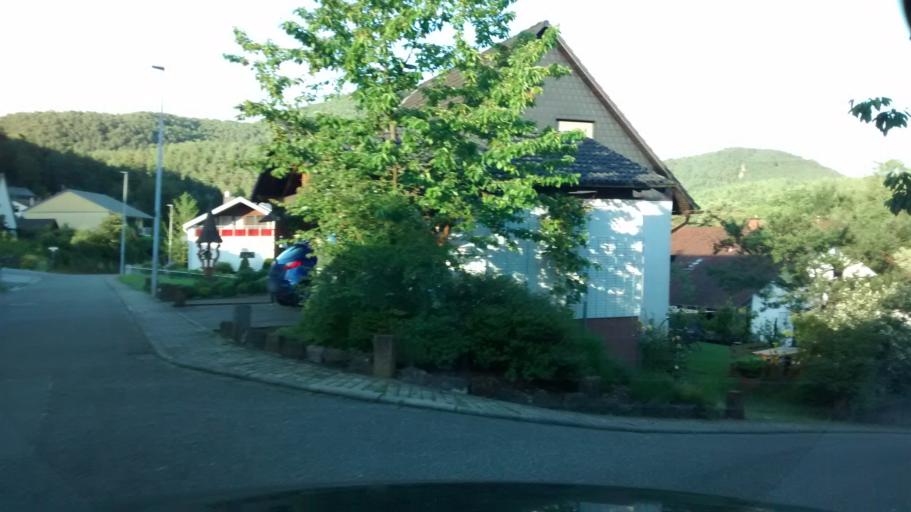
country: DE
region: Rheinland-Pfalz
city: Erfweiler
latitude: 49.1564
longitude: 7.8156
